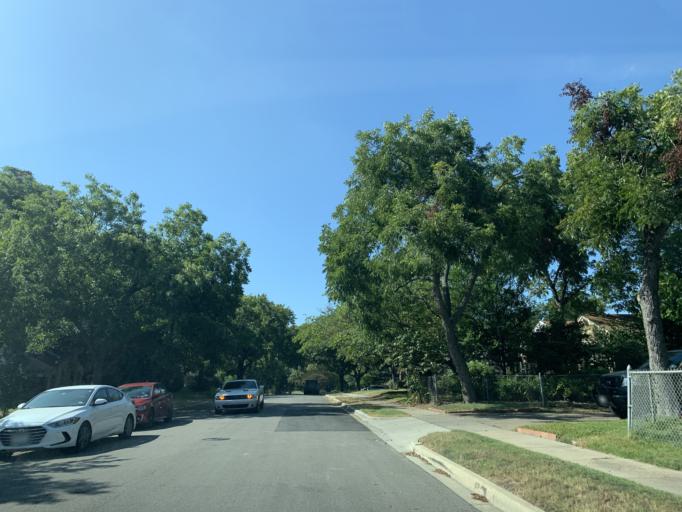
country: US
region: Texas
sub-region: Dallas County
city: Cockrell Hill
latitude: 32.7448
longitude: -96.8656
